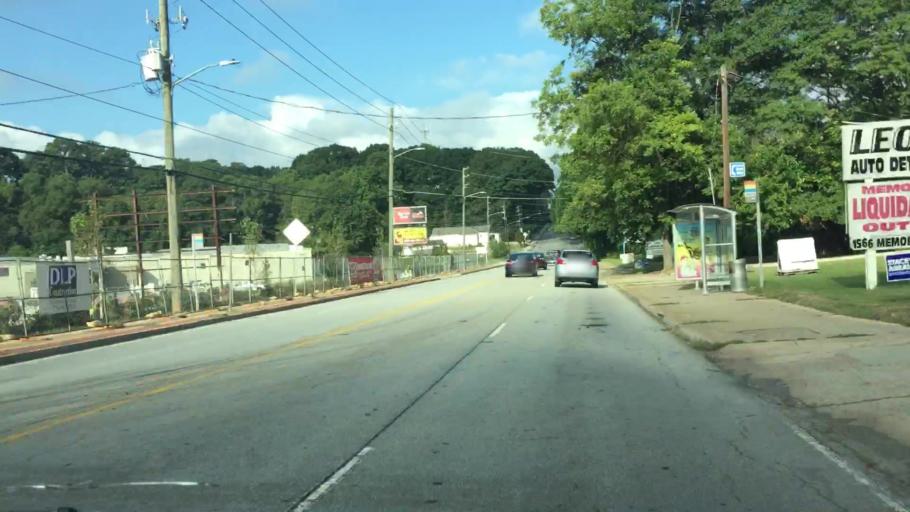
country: US
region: Georgia
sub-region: DeKalb County
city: Druid Hills
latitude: 33.7475
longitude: -84.3356
